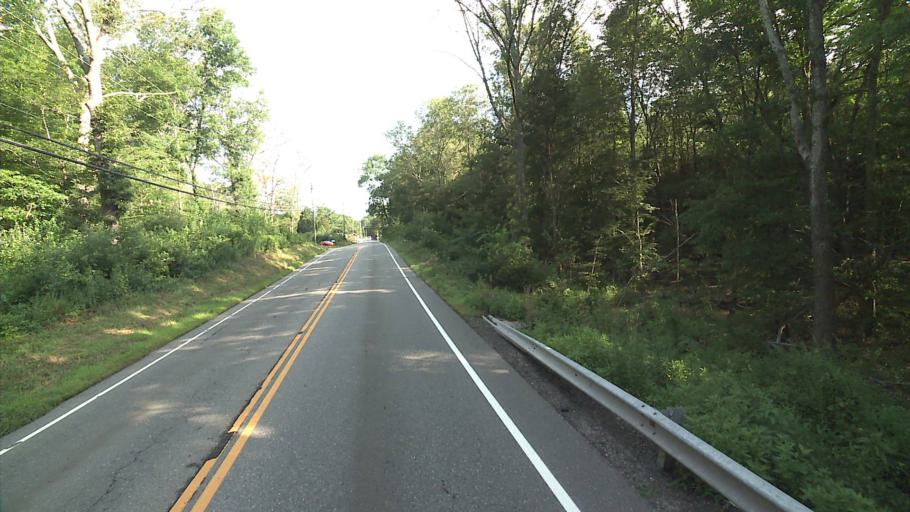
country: US
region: Connecticut
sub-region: New London County
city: Pawcatuck
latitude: 41.4205
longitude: -71.8584
